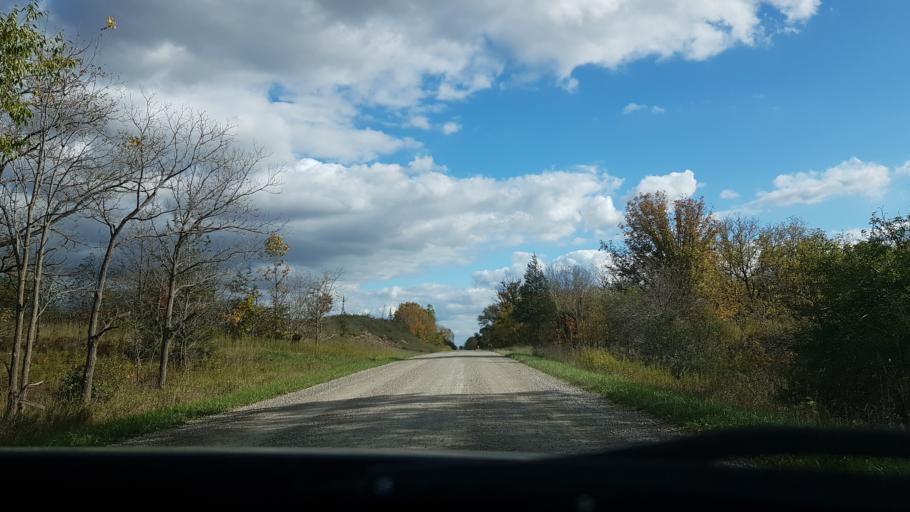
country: CA
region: Ontario
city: South Huron
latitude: 43.0898
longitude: -81.5860
